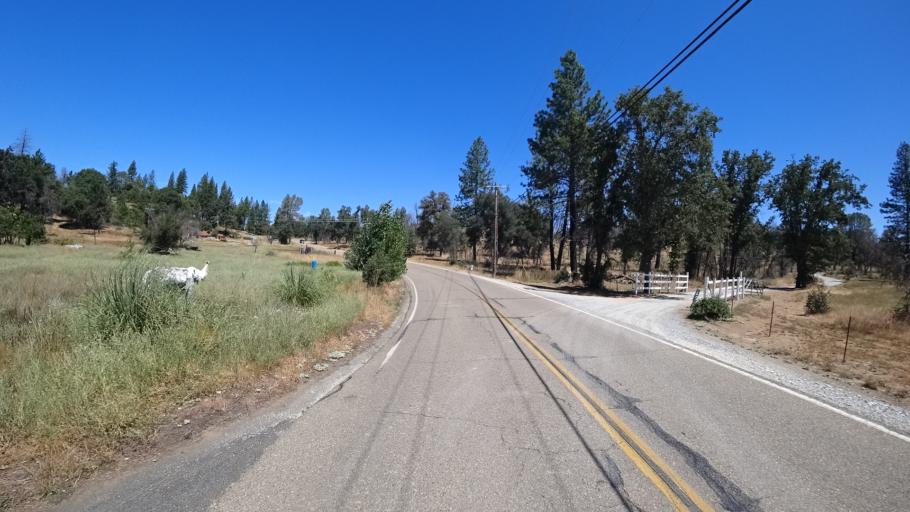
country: US
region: California
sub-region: Calaveras County
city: Mountain Ranch
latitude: 38.2519
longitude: -120.5203
